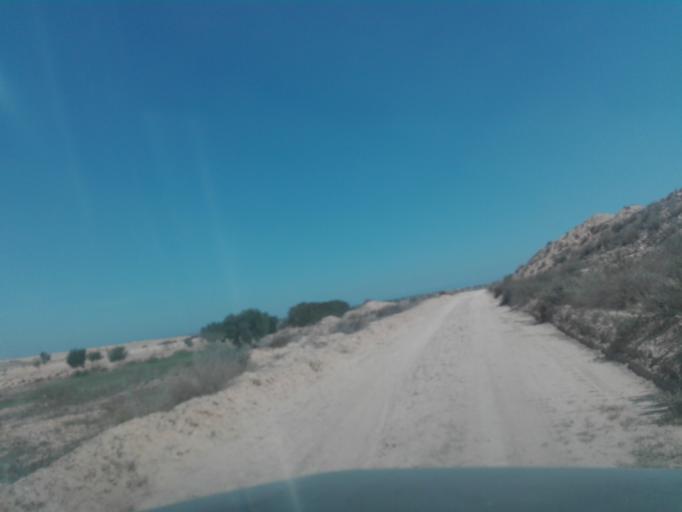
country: TN
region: Qabis
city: Gabes
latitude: 33.8472
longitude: 9.9938
